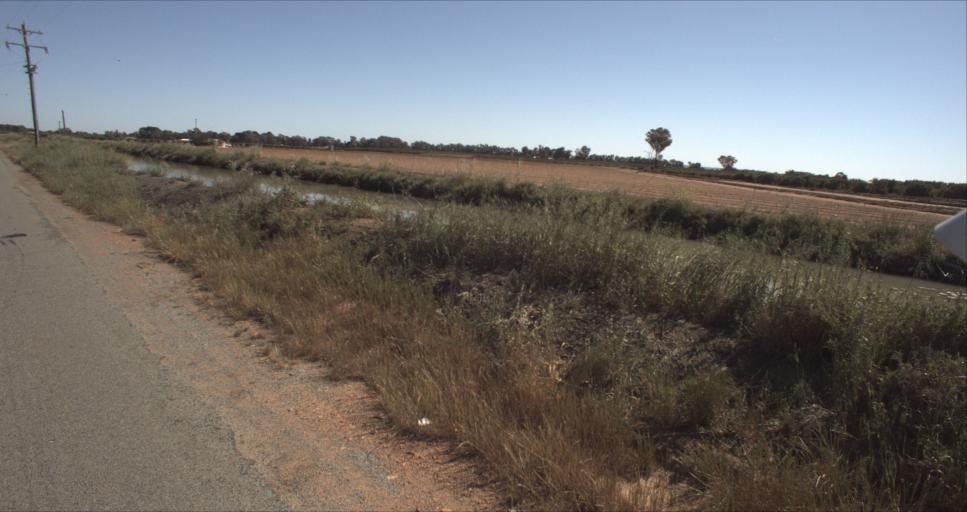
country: AU
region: New South Wales
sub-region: Leeton
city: Leeton
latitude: -34.5406
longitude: 146.3409
